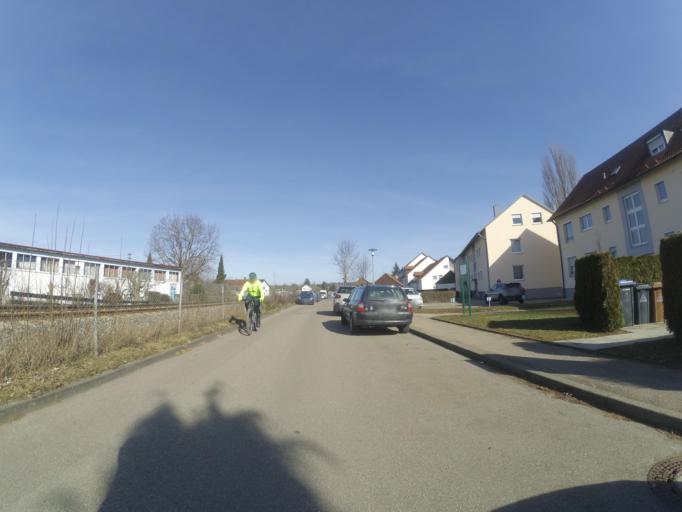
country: DE
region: Baden-Wuerttemberg
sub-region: Regierungsbezirk Stuttgart
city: Niederstotzingen
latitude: 48.5349
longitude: 10.2399
